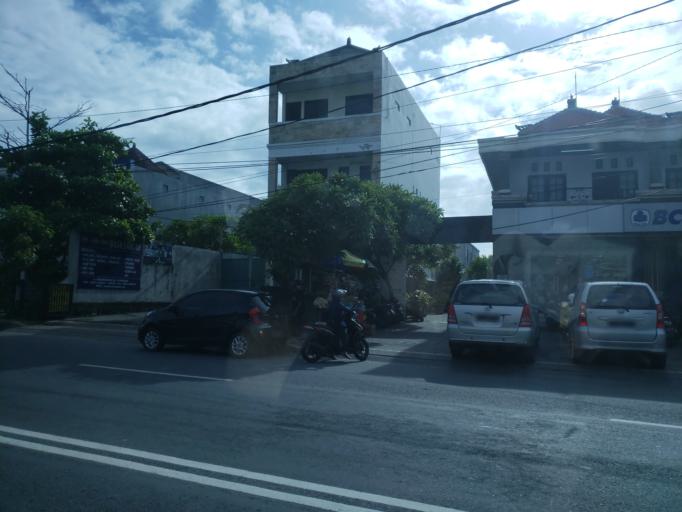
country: ID
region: Bali
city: Denpasar
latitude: -8.6778
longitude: 115.1906
